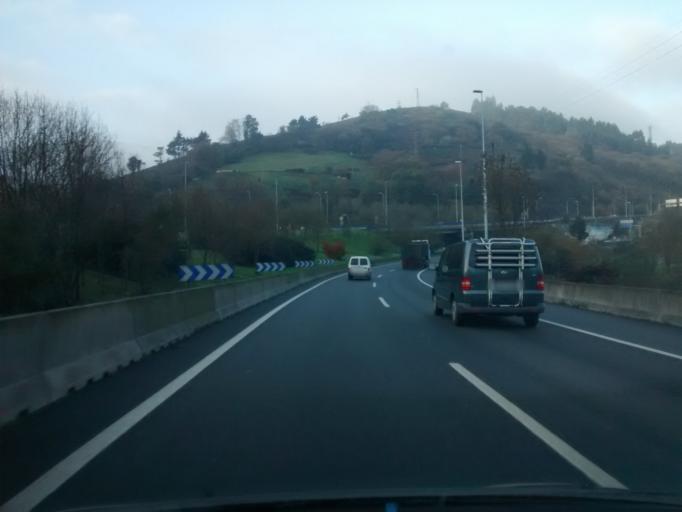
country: ES
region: Basque Country
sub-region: Bizkaia
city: Santutxu
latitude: 43.2333
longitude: -2.9129
